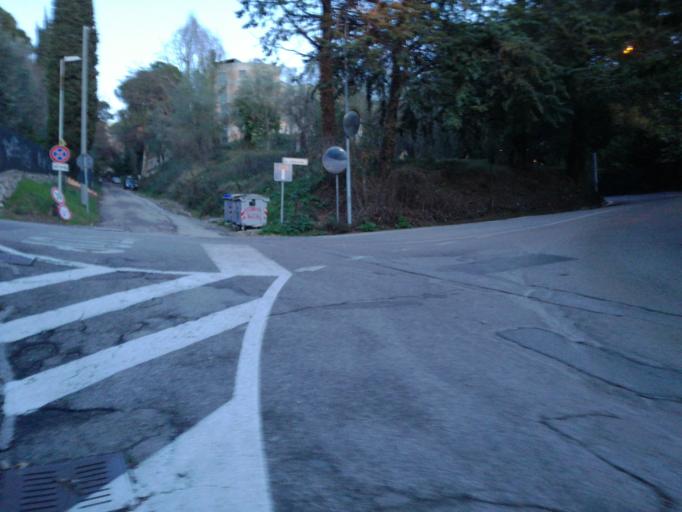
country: IT
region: Umbria
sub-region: Provincia di Perugia
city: Perugia
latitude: 43.1105
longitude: 12.3802
